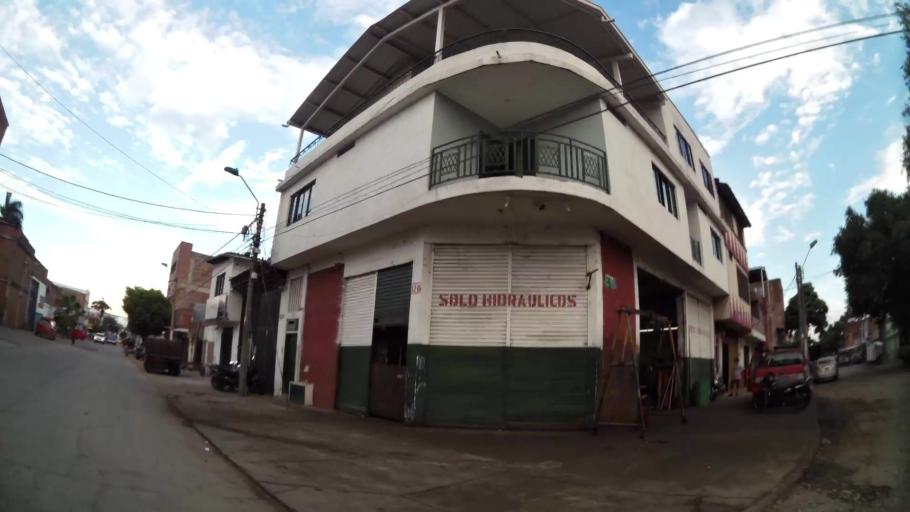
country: CO
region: Valle del Cauca
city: Cali
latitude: 3.4613
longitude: -76.5155
